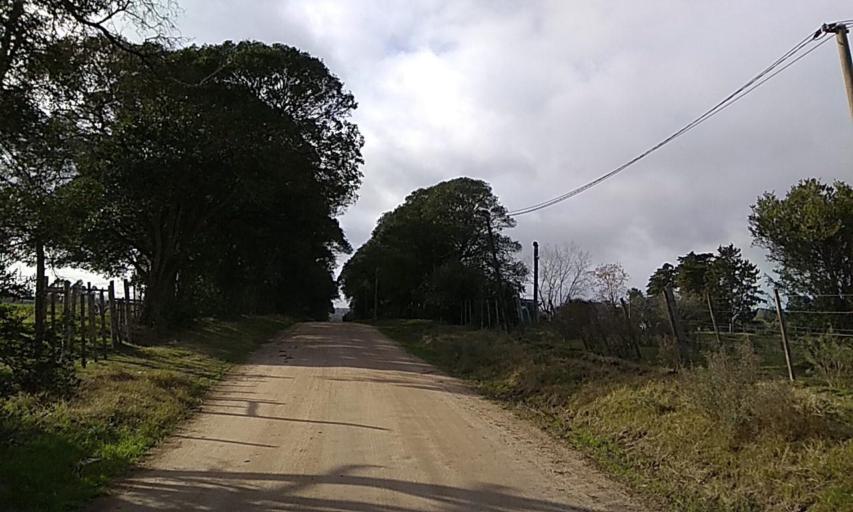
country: UY
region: Florida
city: Florida
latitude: -34.0789
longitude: -56.2153
